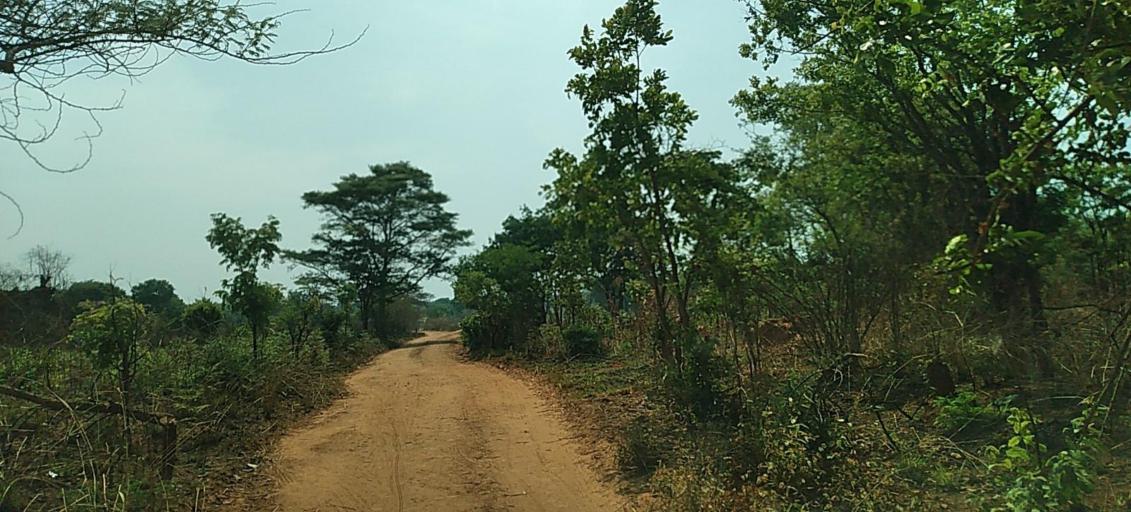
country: ZM
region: Copperbelt
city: Ndola
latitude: -13.2094
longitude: 28.7336
